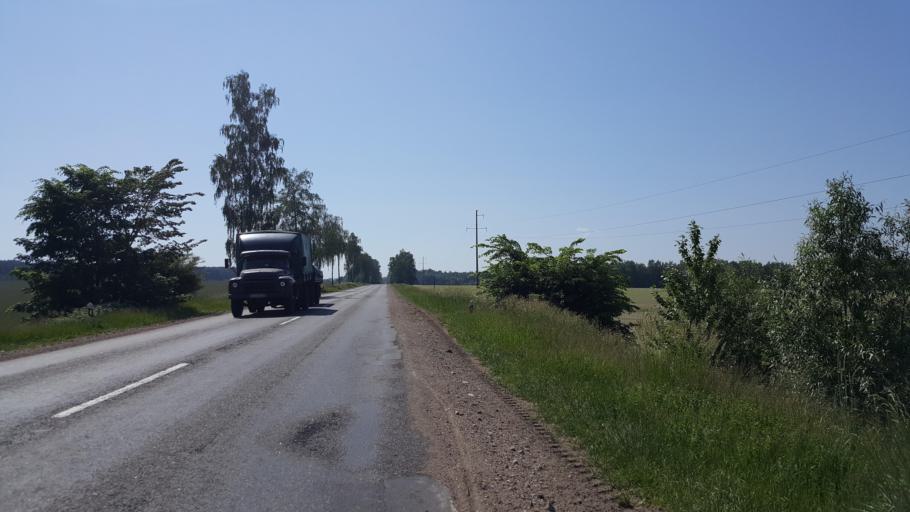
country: BY
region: Brest
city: Zhabinka
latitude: 52.2517
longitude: 23.9691
